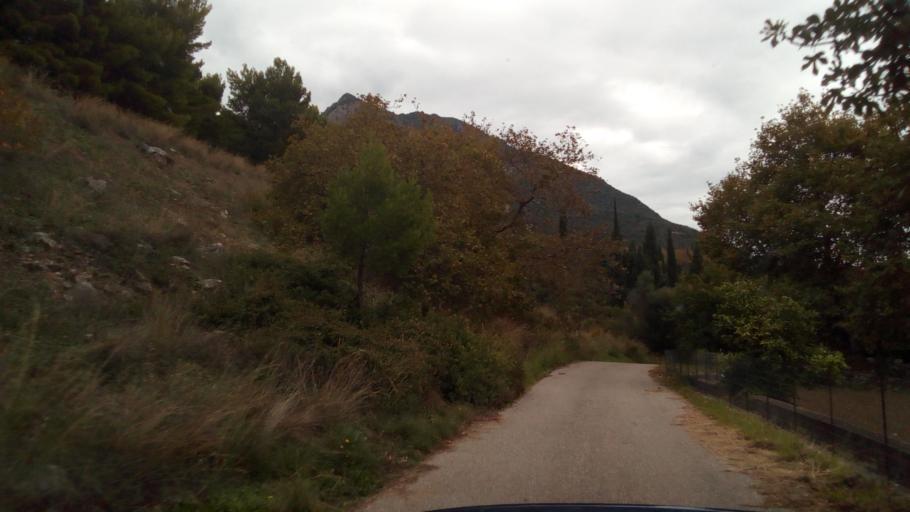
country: GR
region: West Greece
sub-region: Nomos Achaias
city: Kamarai
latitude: 38.3952
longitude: 22.0588
